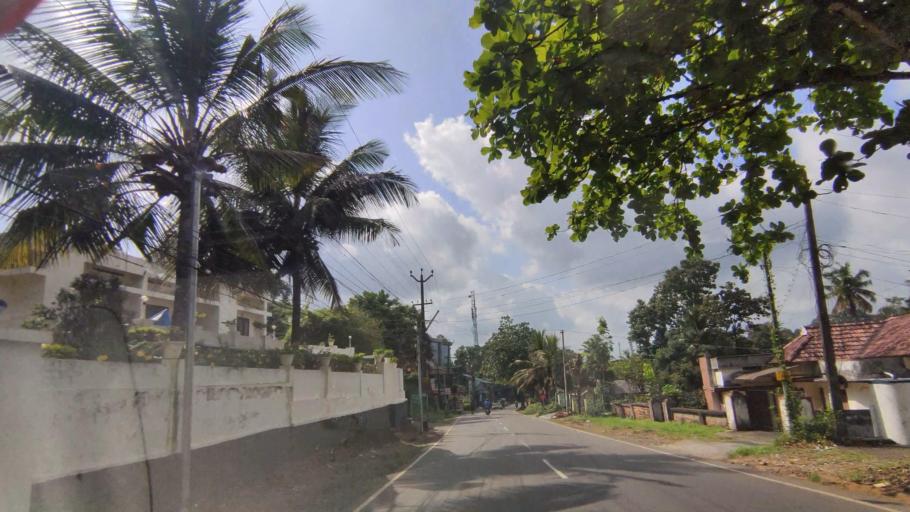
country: IN
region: Kerala
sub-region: Kottayam
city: Kottayam
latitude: 9.6723
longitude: 76.5541
